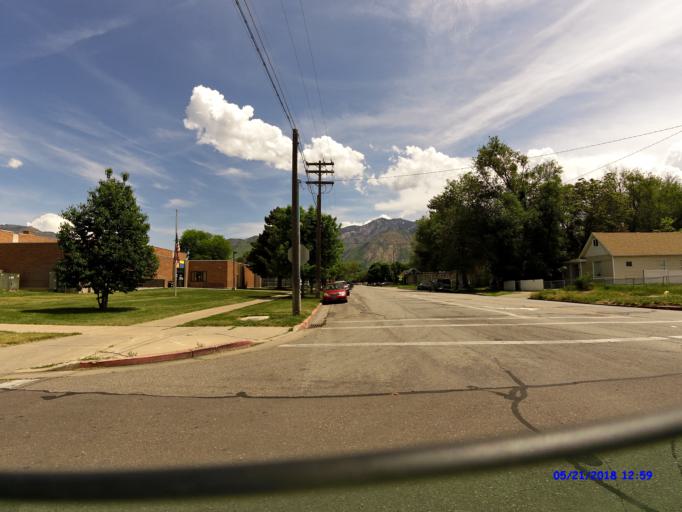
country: US
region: Utah
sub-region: Weber County
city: Ogden
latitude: 41.2145
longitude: -111.9762
